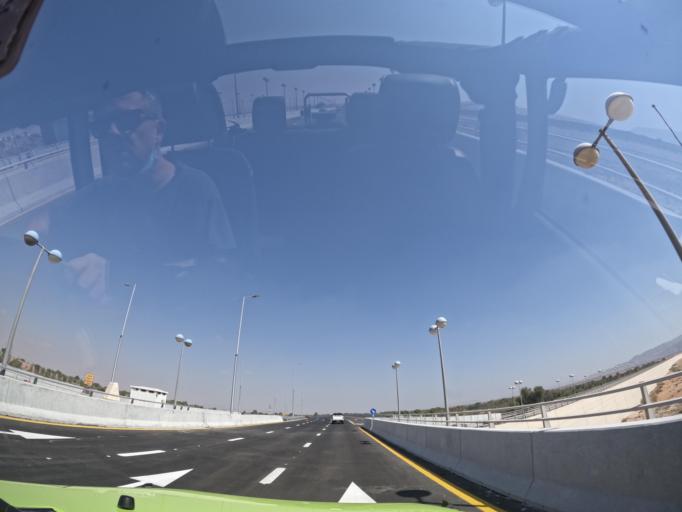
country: AE
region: Ash Shariqah
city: Adh Dhayd
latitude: 24.7825
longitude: 55.8156
